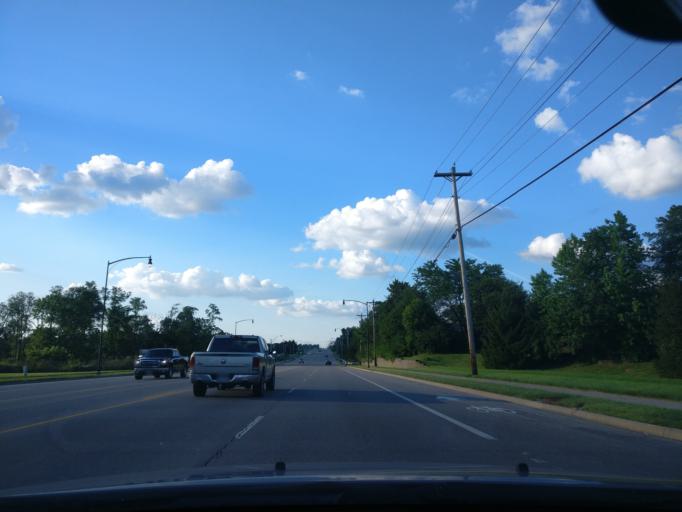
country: US
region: Ohio
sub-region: Warren County
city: Springboro
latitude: 39.5660
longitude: -84.2319
